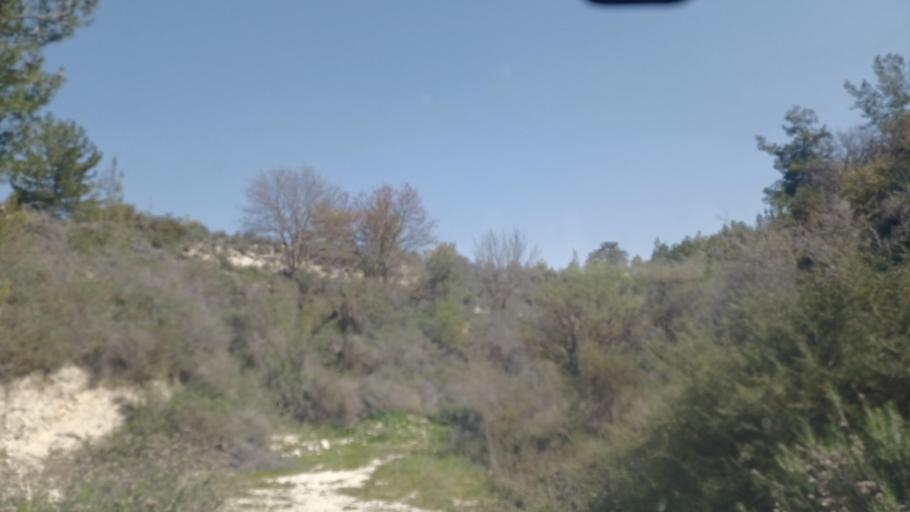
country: CY
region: Limassol
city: Pachna
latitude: 34.8608
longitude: 32.7360
